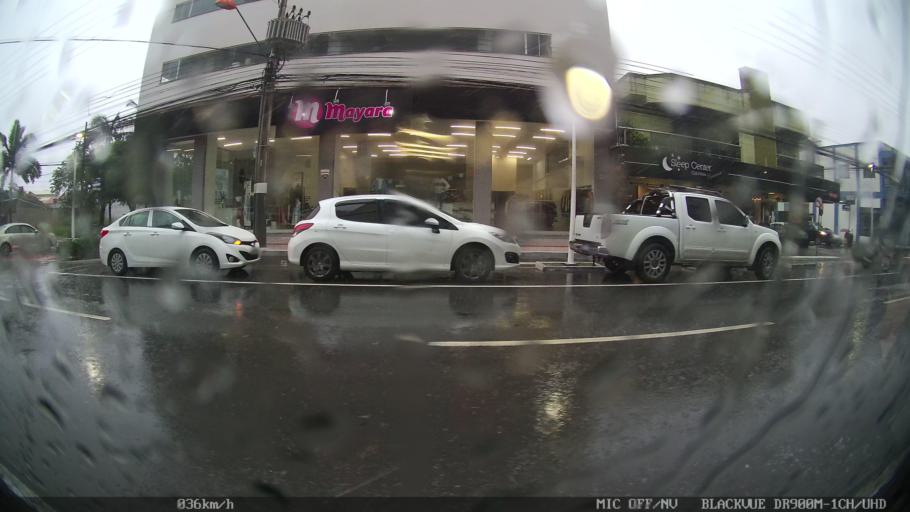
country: BR
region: Santa Catarina
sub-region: Balneario Camboriu
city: Balneario Camboriu
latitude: -26.9991
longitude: -48.6318
